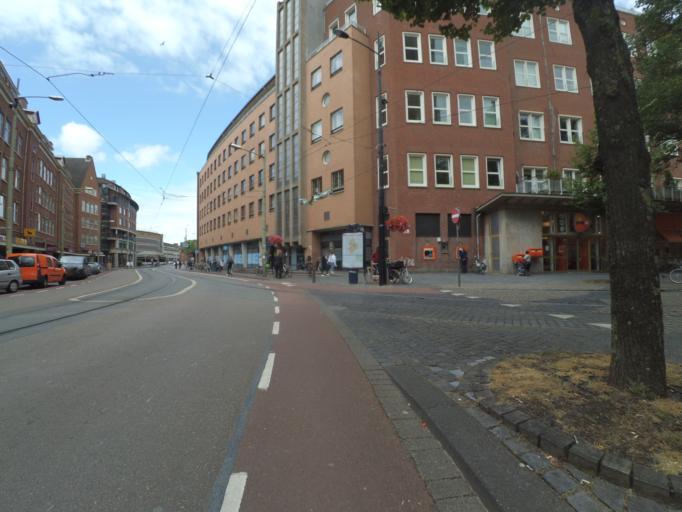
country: NL
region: South Holland
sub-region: Gemeente Den Haag
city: The Hague
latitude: 52.0774
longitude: 4.3064
